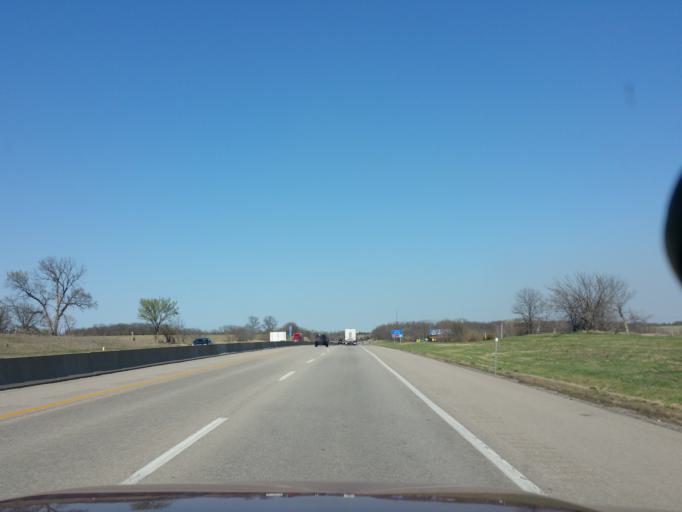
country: US
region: Kansas
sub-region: Douglas County
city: Lawrence
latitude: 39.0021
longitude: -95.1746
